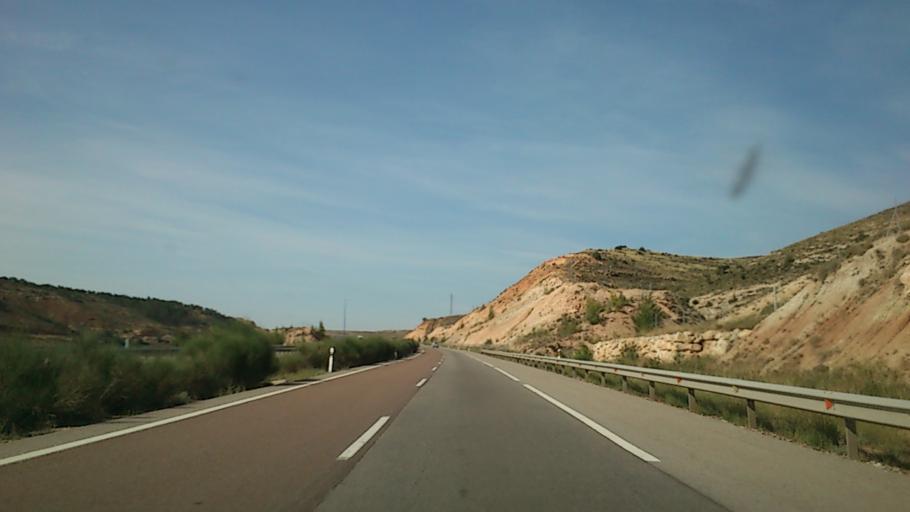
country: ES
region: Aragon
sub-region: Provincia de Teruel
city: Calamocha
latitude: 40.9849
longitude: -1.2593
